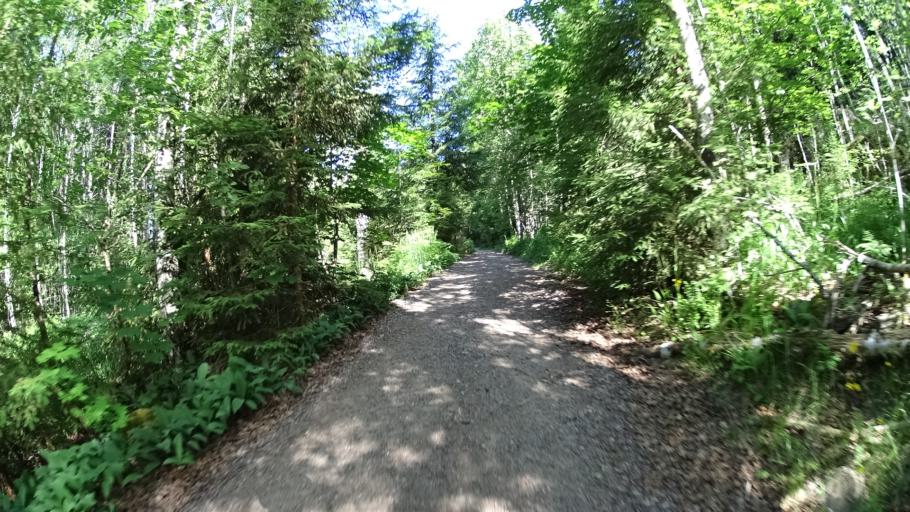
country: FI
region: Uusimaa
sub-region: Helsinki
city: Espoo
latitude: 60.3135
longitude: 24.5091
